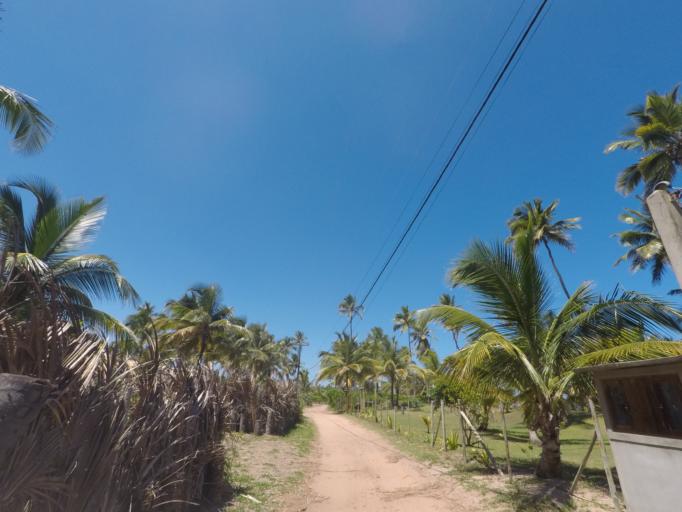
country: BR
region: Bahia
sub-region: Marau
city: Marau
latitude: -14.0002
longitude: -38.9445
